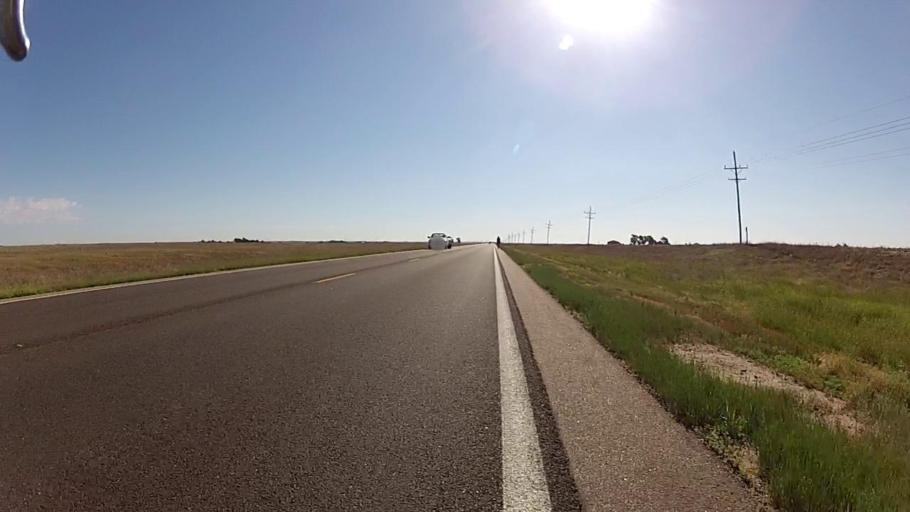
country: US
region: Kansas
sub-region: Haskell County
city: Sublette
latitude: 37.5497
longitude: -100.6045
